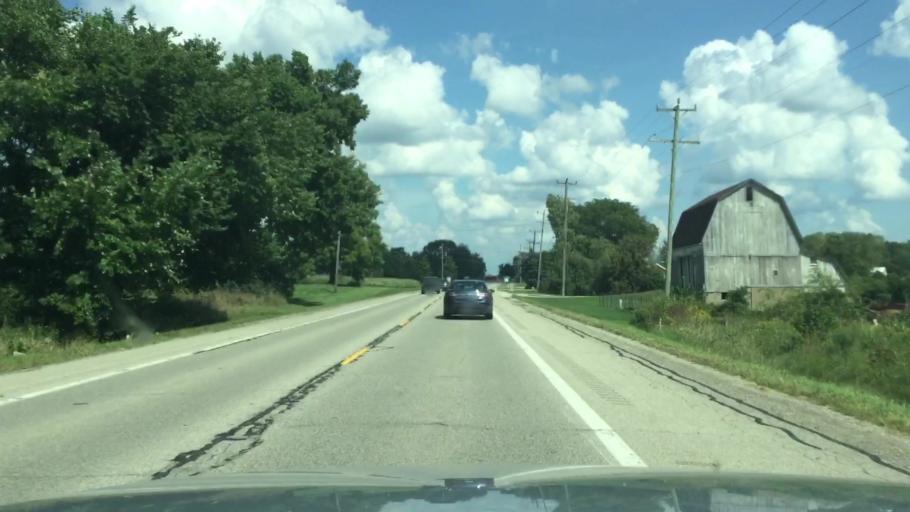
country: US
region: Michigan
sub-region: Washtenaw County
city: Saline
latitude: 42.1466
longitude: -83.8295
